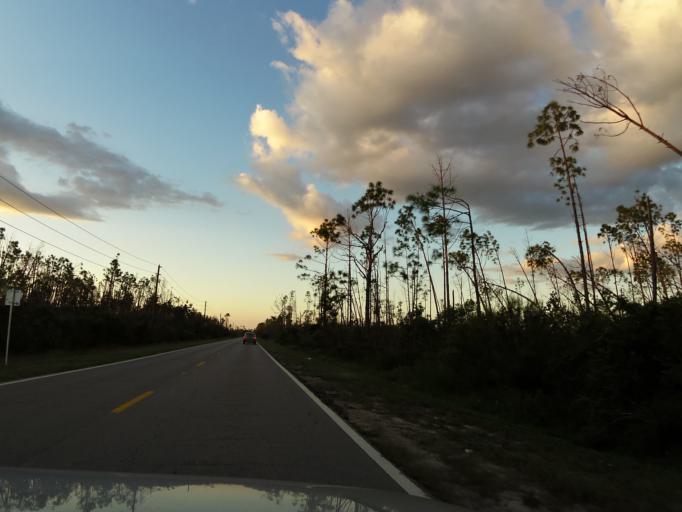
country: US
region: Florida
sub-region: Bay County
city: Mexico Beach
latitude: 29.9338
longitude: -85.3885
